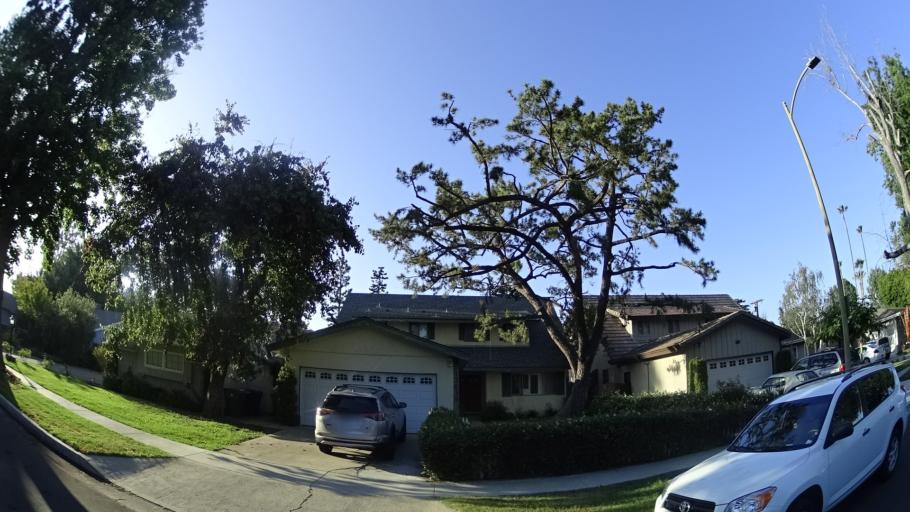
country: US
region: California
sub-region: Los Angeles County
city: Van Nuys
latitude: 34.1695
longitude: -118.4346
